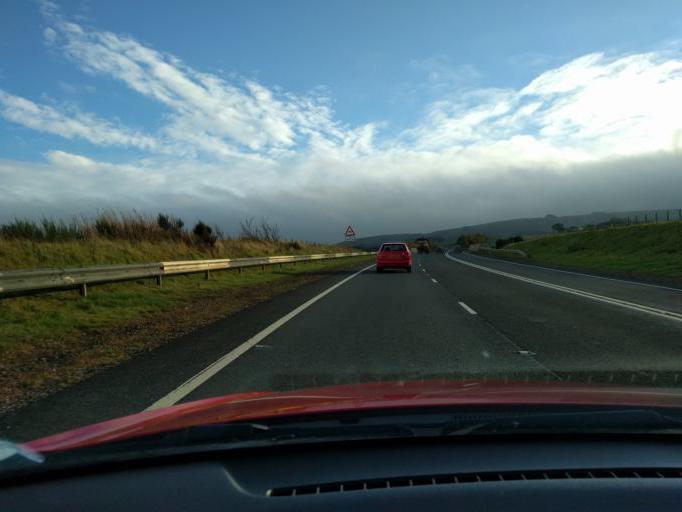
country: GB
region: Scotland
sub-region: The Scottish Borders
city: Duns
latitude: 55.9358
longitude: -2.3564
